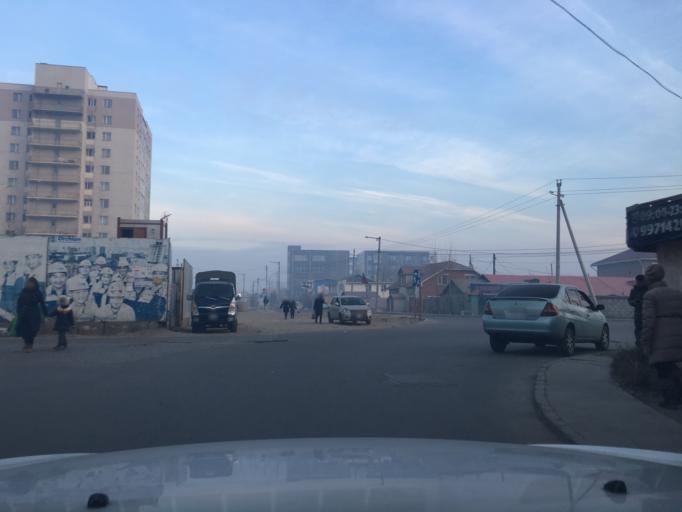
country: MN
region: Ulaanbaatar
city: Ulaanbaatar
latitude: 47.9235
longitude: 106.8121
